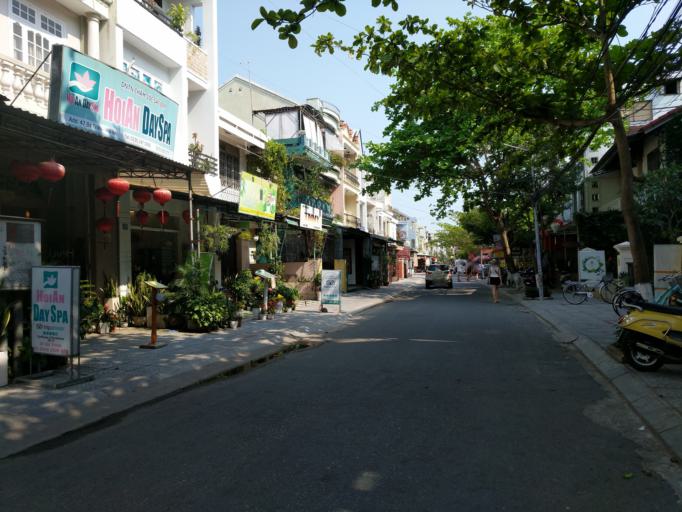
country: VN
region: Quang Nam
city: Hoi An
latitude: 15.8820
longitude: 108.3247
